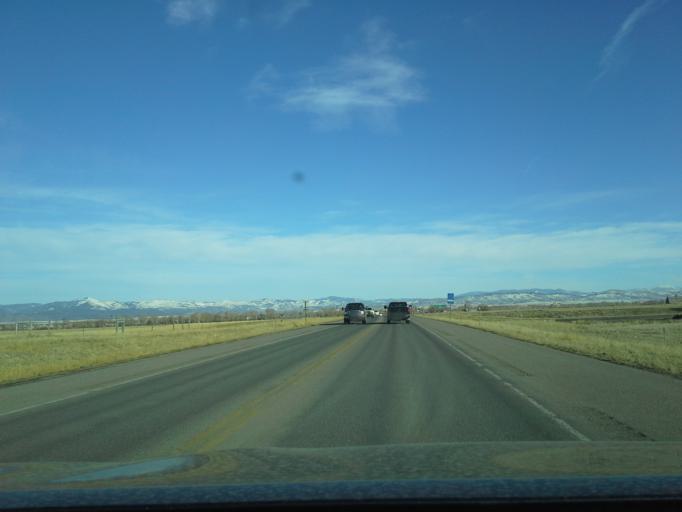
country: US
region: Montana
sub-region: Lewis and Clark County
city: Helena Valley Southeast
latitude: 46.6163
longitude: -111.9812
